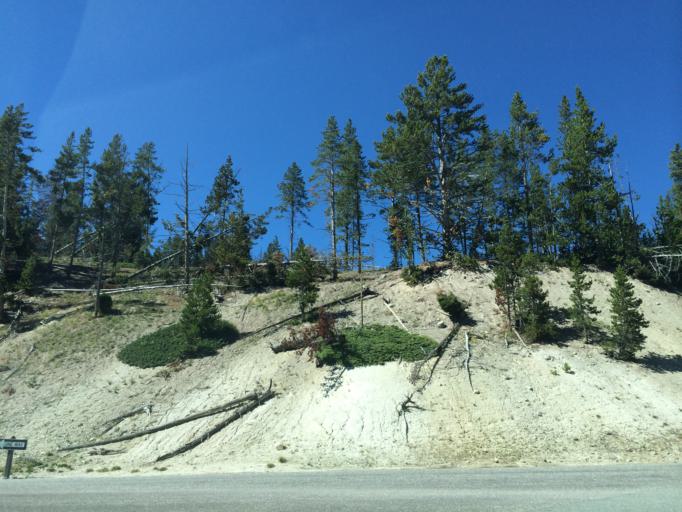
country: US
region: Montana
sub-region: Gallatin County
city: West Yellowstone
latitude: 44.6257
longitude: -110.4332
